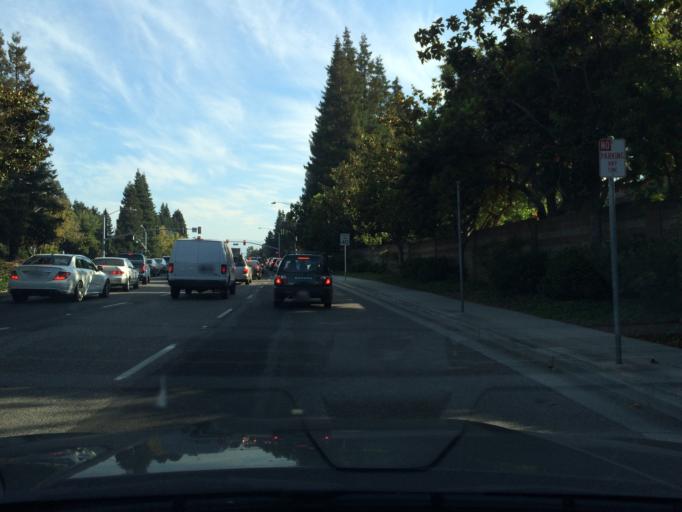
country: US
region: California
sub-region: Santa Clara County
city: Sunnyvale
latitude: 37.3881
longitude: -122.0431
